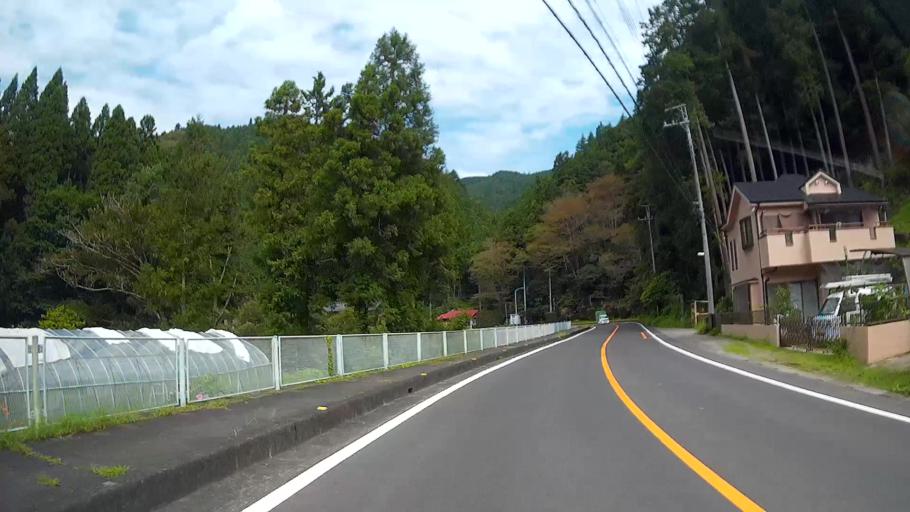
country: JP
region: Tokyo
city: Ome
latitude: 35.8567
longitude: 139.2083
